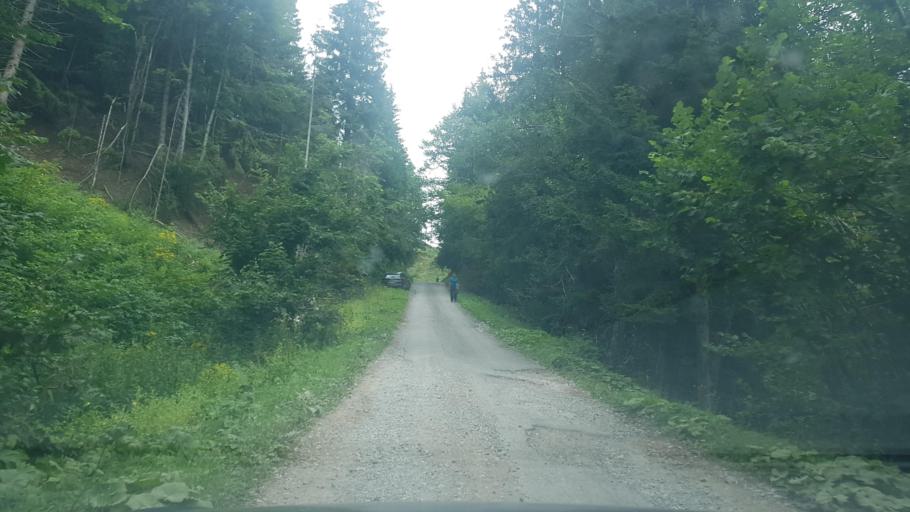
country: IT
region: Friuli Venezia Giulia
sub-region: Provincia di Udine
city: Rigolato
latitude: 46.5525
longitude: 12.8188
